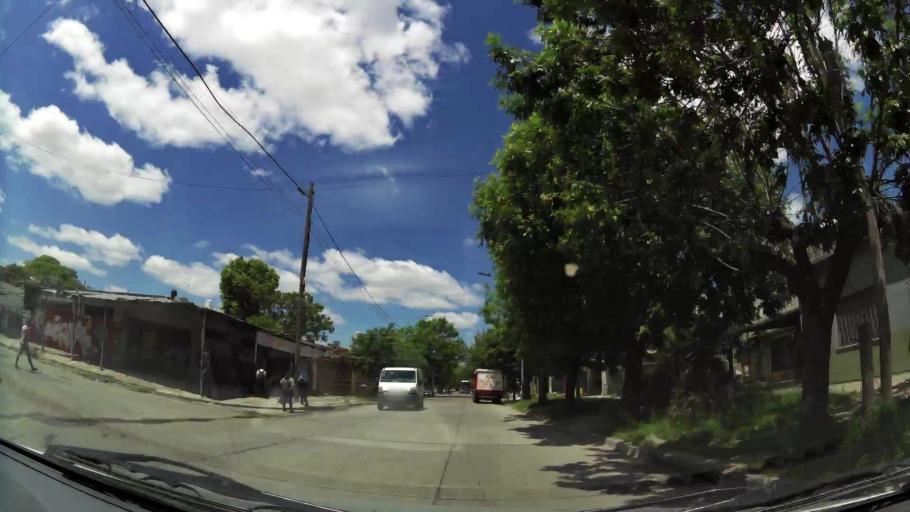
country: AR
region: Buenos Aires
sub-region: Partido de Lanus
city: Lanus
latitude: -34.7180
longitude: -58.4129
